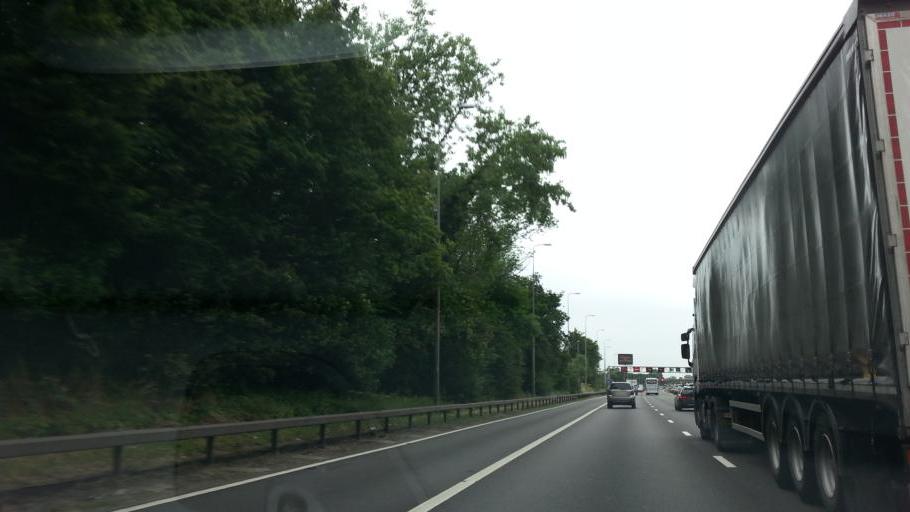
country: GB
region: England
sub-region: Solihull
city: Bickenhill
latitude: 52.4232
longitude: -1.7204
